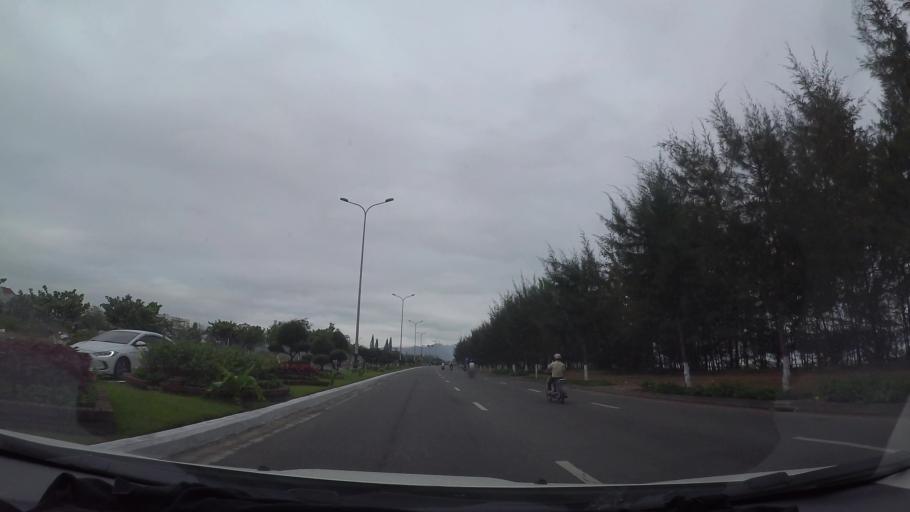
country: VN
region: Da Nang
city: Lien Chieu
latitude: 16.0911
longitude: 108.1509
